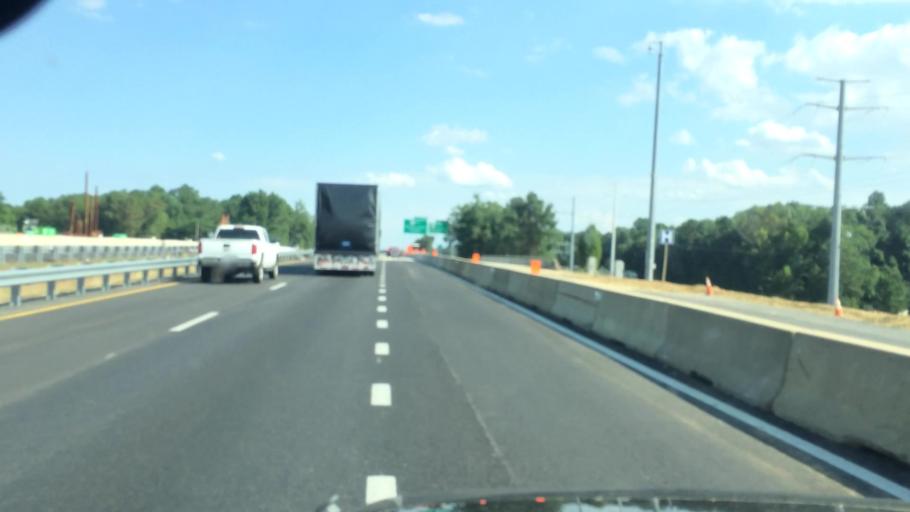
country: US
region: Virginia
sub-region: City of Williamsburg
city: Williamsburg
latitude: 37.2618
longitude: -76.6493
